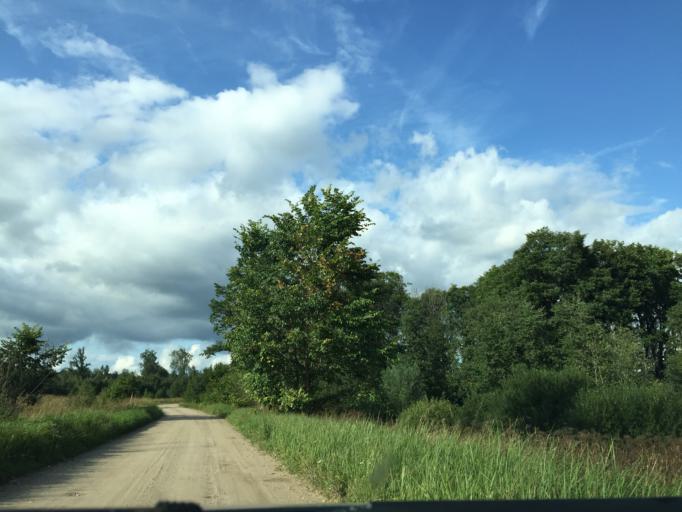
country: LV
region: Kegums
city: Kegums
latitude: 56.8213
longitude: 24.7568
